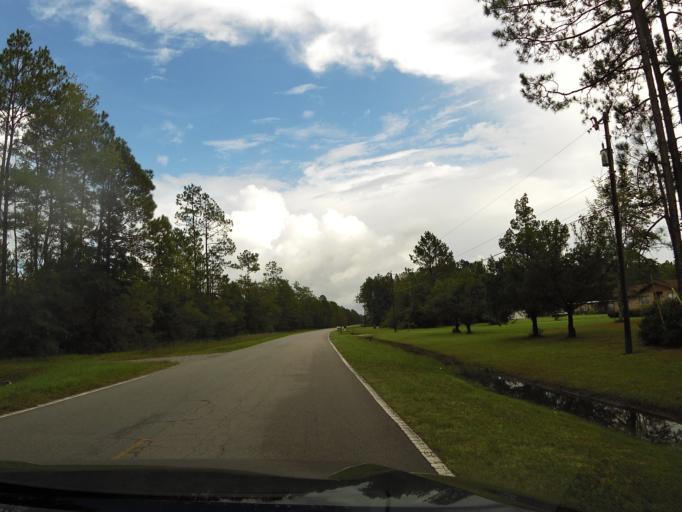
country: US
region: Florida
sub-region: Duval County
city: Baldwin
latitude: 30.3958
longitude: -81.9496
